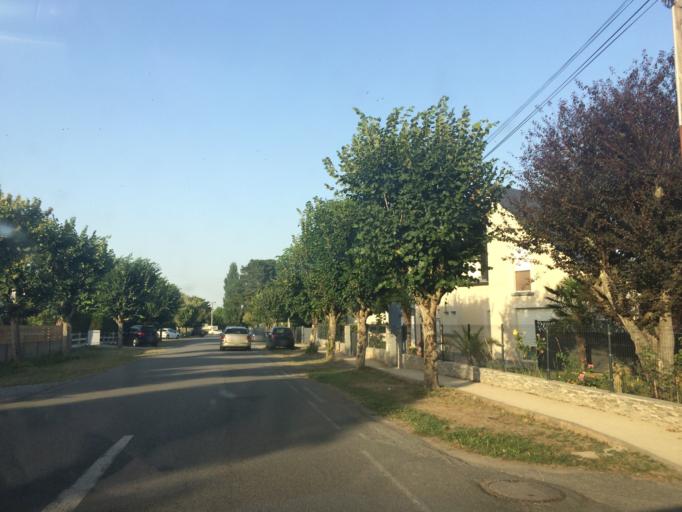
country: FR
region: Brittany
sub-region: Departement du Morbihan
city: Damgan
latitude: 47.5158
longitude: -2.5522
